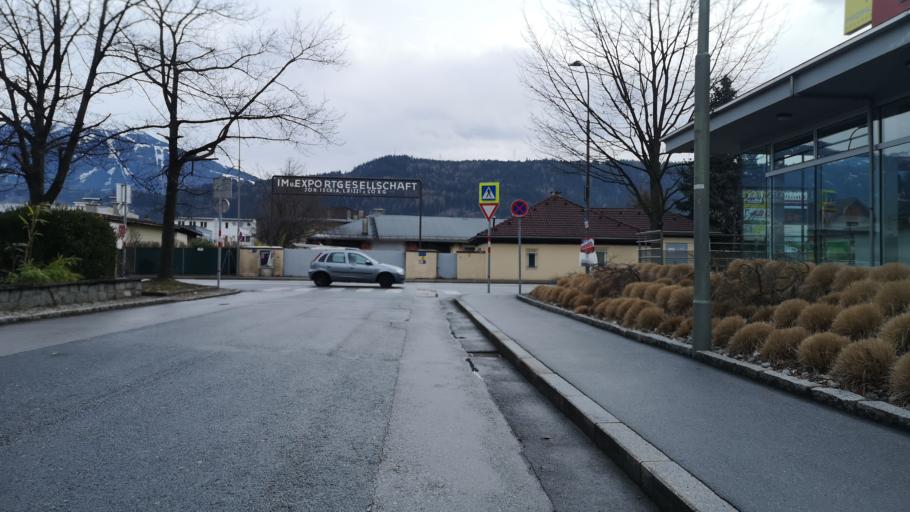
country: AT
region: Tyrol
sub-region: Innsbruck Stadt
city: Innsbruck
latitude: 47.2626
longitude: 11.3716
